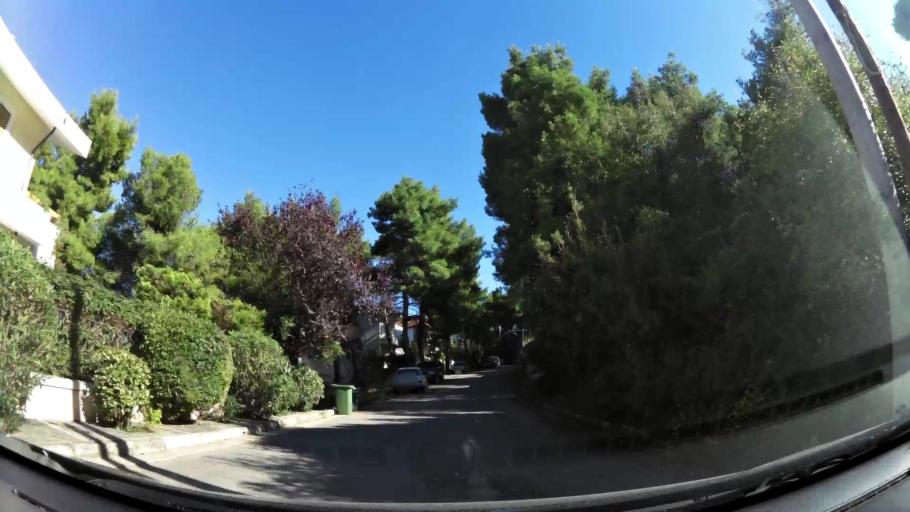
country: GR
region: Attica
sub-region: Nomarchia Anatolikis Attikis
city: Rodopoli
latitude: 38.1126
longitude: 23.8761
